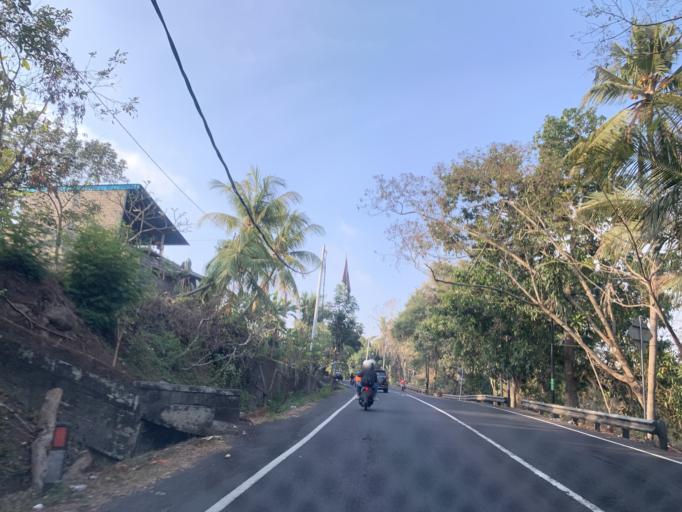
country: ID
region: Bali
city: Banjar Delodrurung
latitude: -8.5000
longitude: 115.0207
